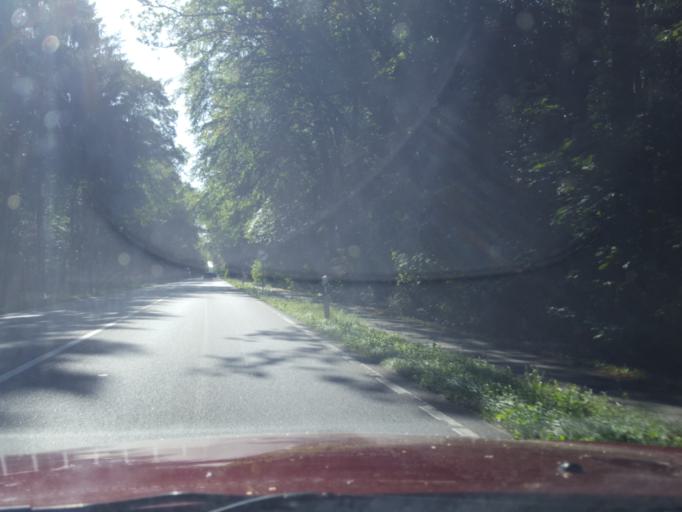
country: DE
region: Lower Saxony
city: Eystrup
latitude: 52.8115
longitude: 9.2016
